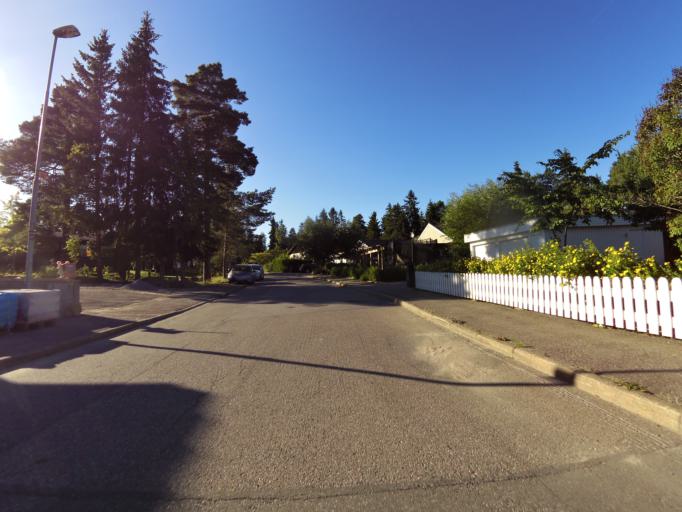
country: SE
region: Gaevleborg
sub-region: Gavle Kommun
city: Gavle
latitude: 60.6538
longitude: 17.1527
